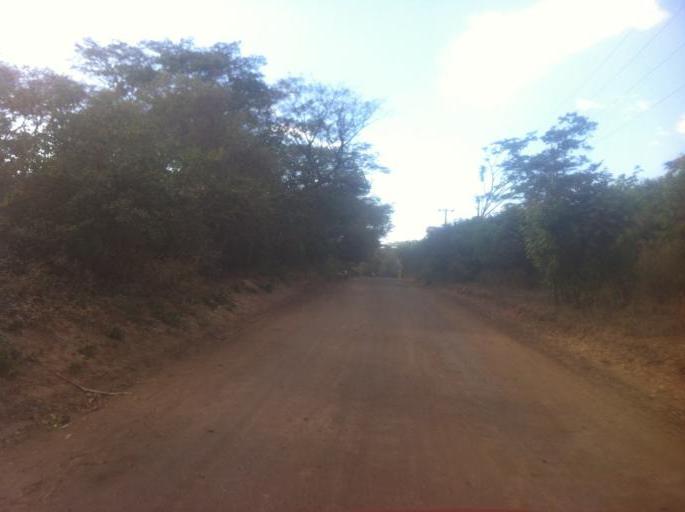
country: NI
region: Managua
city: Masachapa
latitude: 11.8323
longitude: -86.5085
